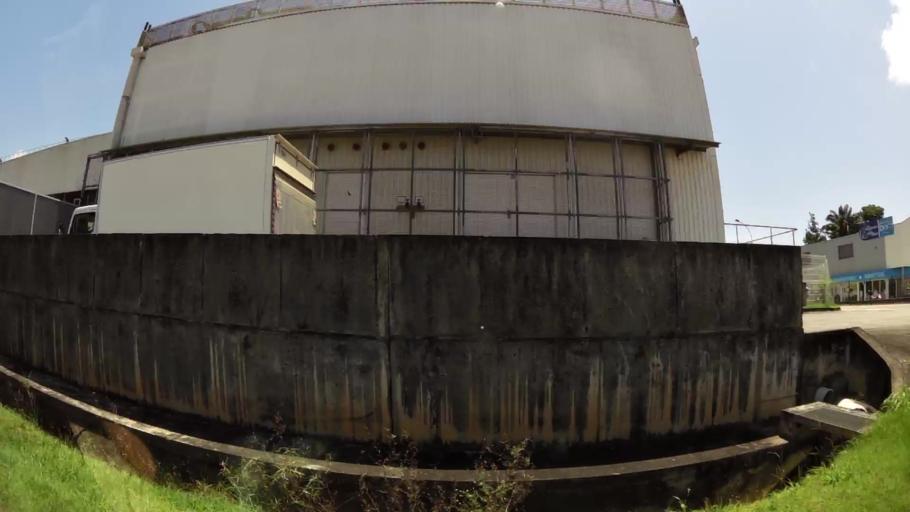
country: GF
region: Guyane
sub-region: Guyane
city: Cayenne
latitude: 4.9030
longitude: -52.3215
